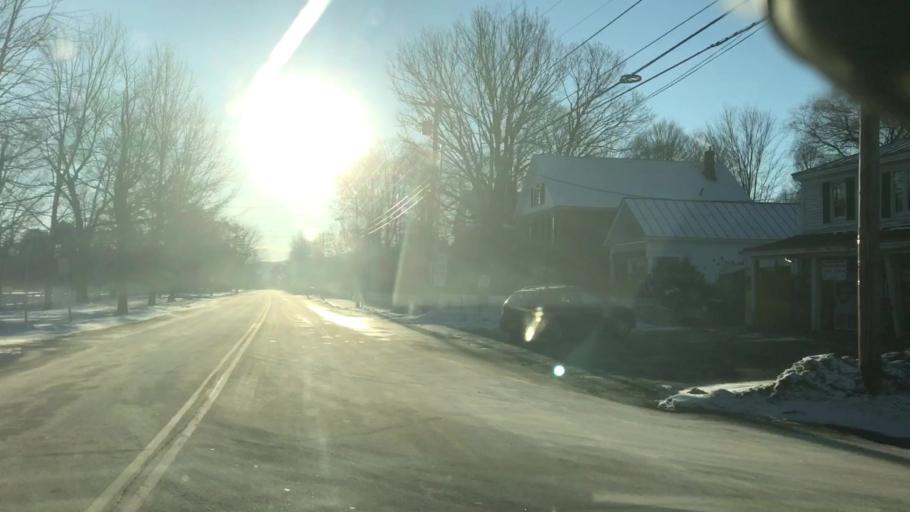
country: US
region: New Hampshire
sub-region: Grafton County
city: Orford
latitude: 43.9052
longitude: -72.1372
